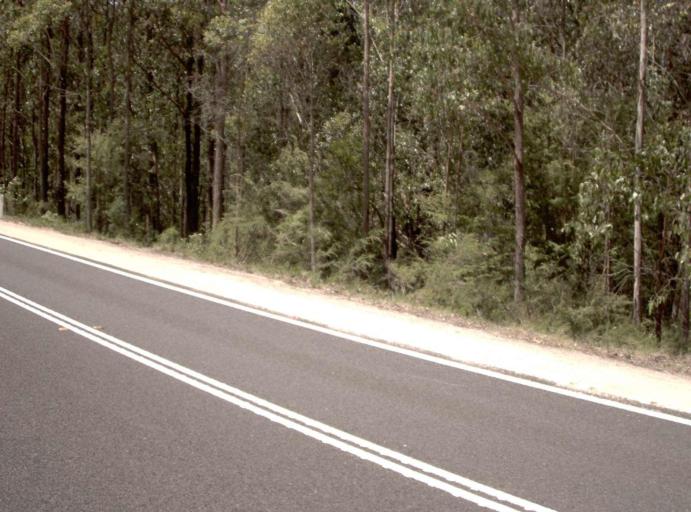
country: AU
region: New South Wales
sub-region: Bombala
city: Bombala
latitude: -37.6205
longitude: 148.8910
